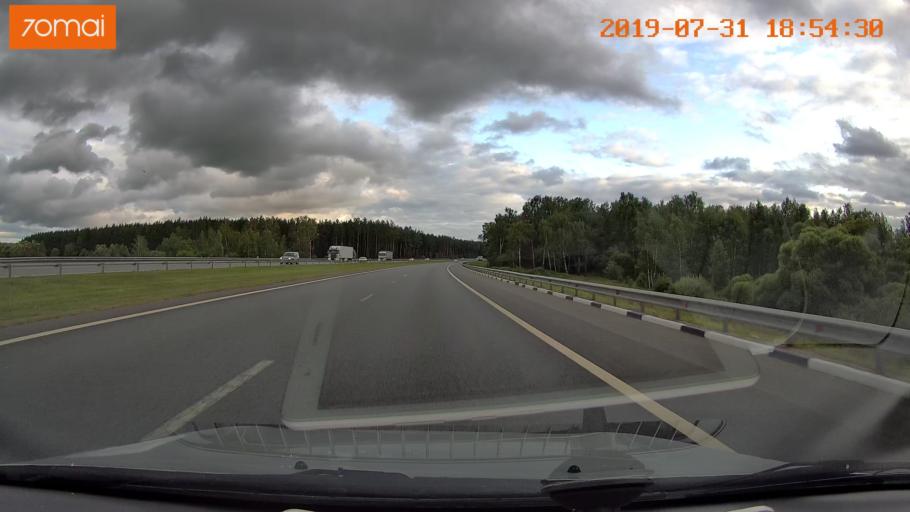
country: RU
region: Moskovskaya
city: Raduzhnyy
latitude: 55.1890
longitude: 38.6684
